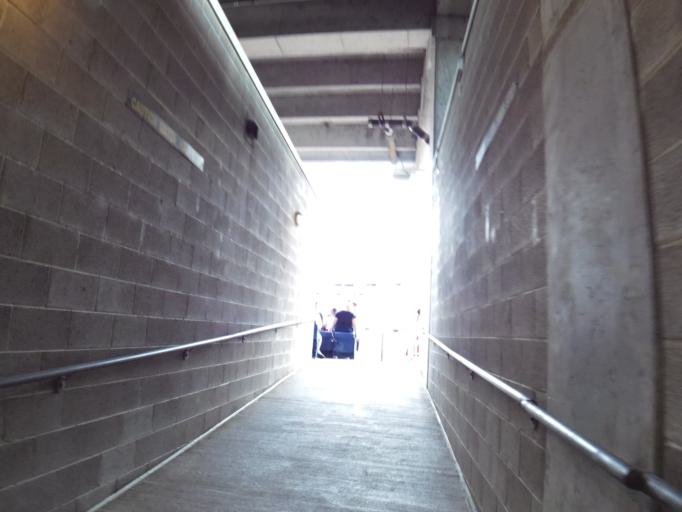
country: US
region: Tennessee
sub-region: Davidson County
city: Nashville
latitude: 36.1661
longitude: -86.7708
